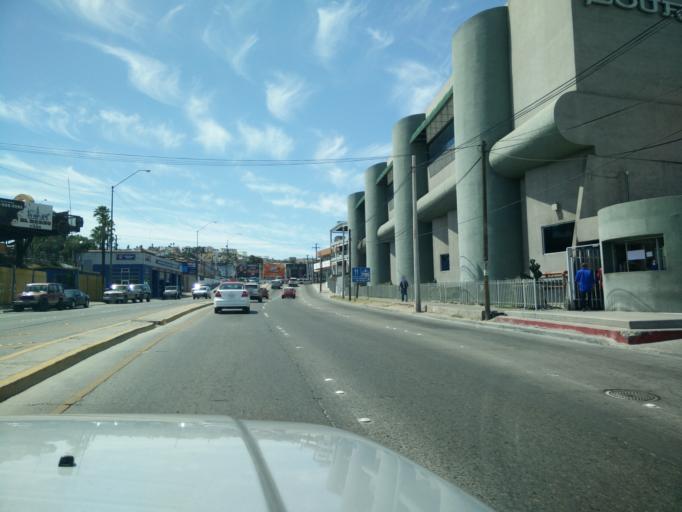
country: MX
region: Baja California
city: Tijuana
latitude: 32.5182
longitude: -117.0124
